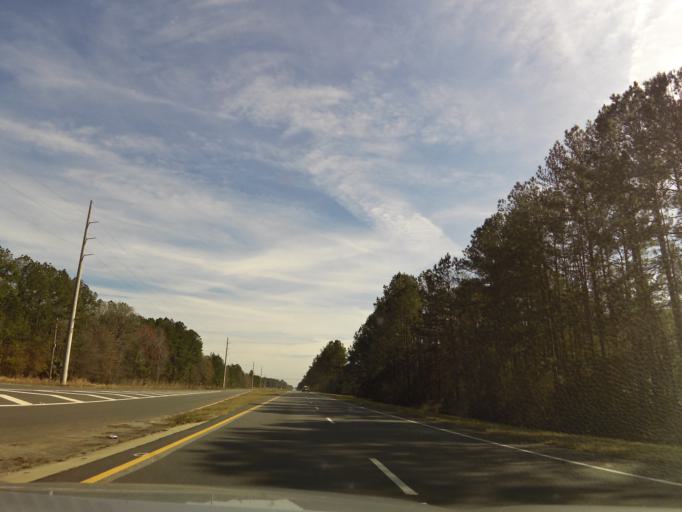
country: US
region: Georgia
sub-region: Glynn County
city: Dock Junction
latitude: 31.2139
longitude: -81.7123
